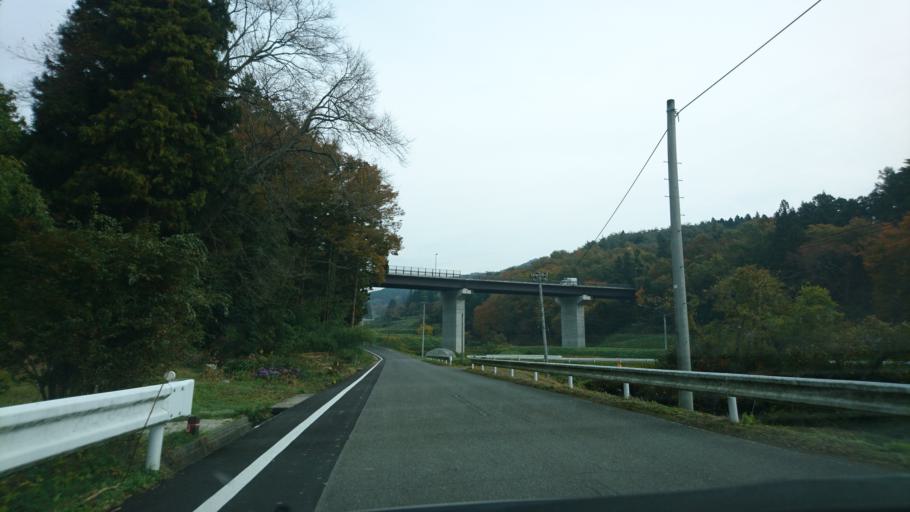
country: JP
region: Iwate
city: Ichinoseki
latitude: 38.9699
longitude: 141.1685
